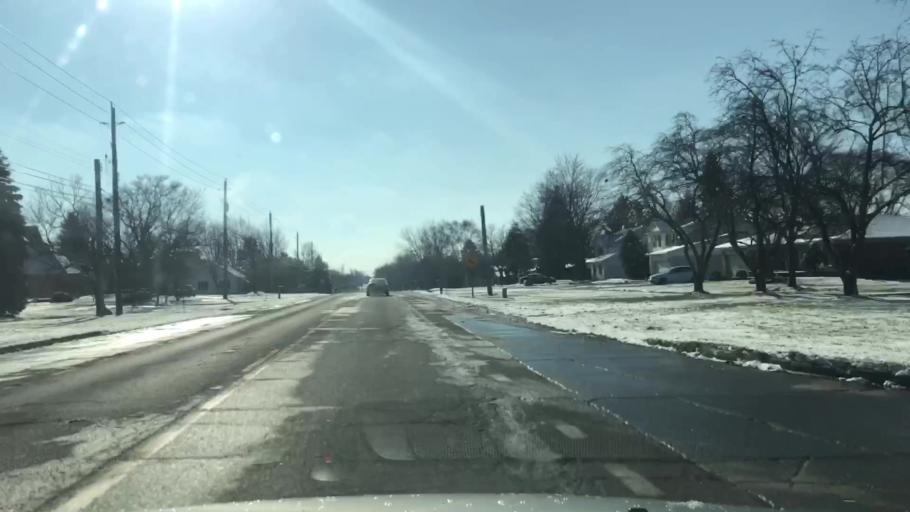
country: US
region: Michigan
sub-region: Oakland County
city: Troy
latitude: 42.6168
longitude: -83.1106
